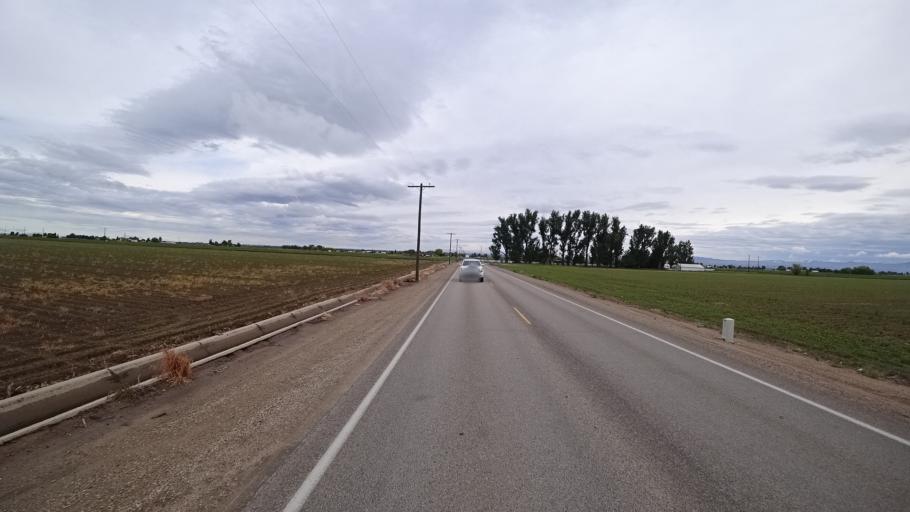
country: US
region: Idaho
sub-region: Ada County
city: Star
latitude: 43.6546
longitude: -116.4936
